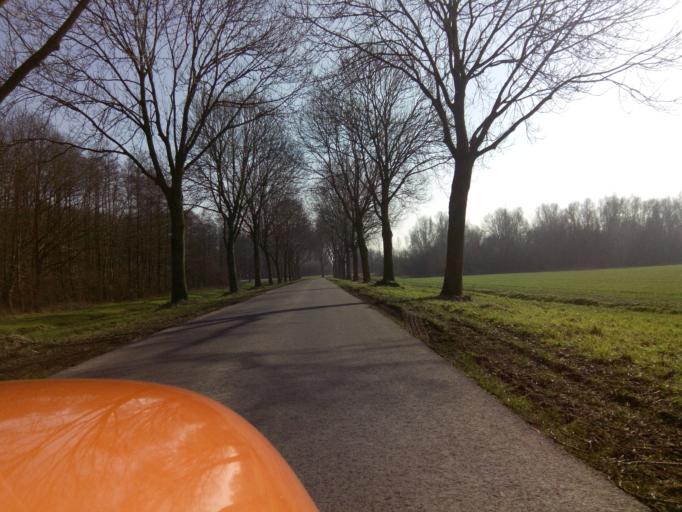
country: NL
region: Gelderland
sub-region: Gemeente Nijkerk
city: Nijkerk
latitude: 52.2692
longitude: 5.4815
